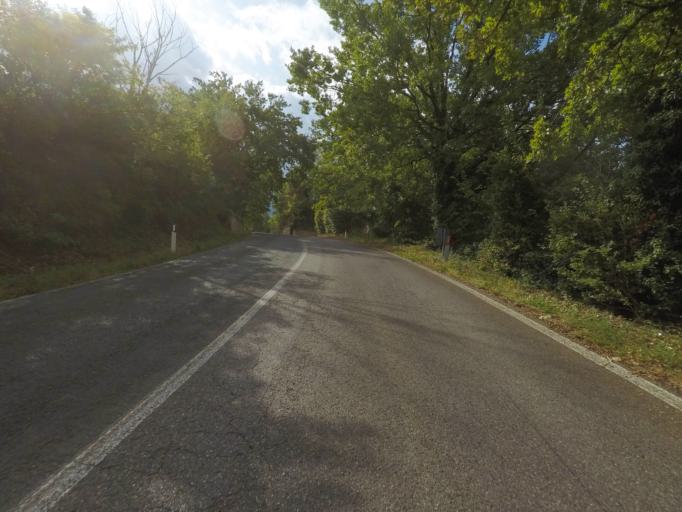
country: IT
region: Tuscany
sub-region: Provincia di Siena
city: Montepulciano
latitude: 43.1149
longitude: 11.7906
